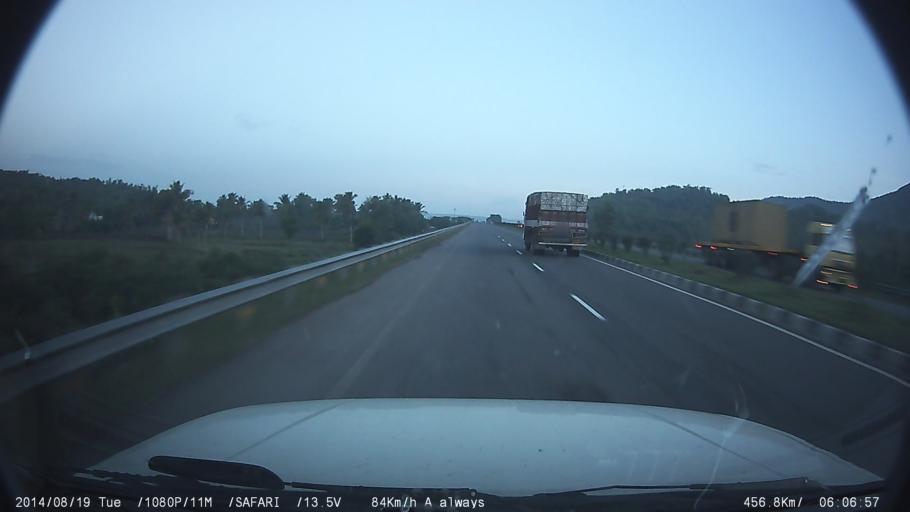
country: IN
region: Tamil Nadu
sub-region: Salem
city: Omalur
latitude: 11.8944
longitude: 78.0667
